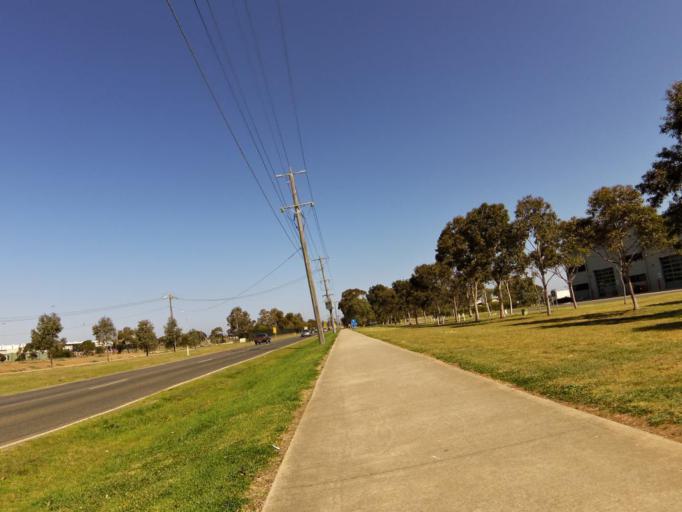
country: AU
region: Victoria
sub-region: Wyndham
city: Hoppers Crossing
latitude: -37.8899
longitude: 144.7006
